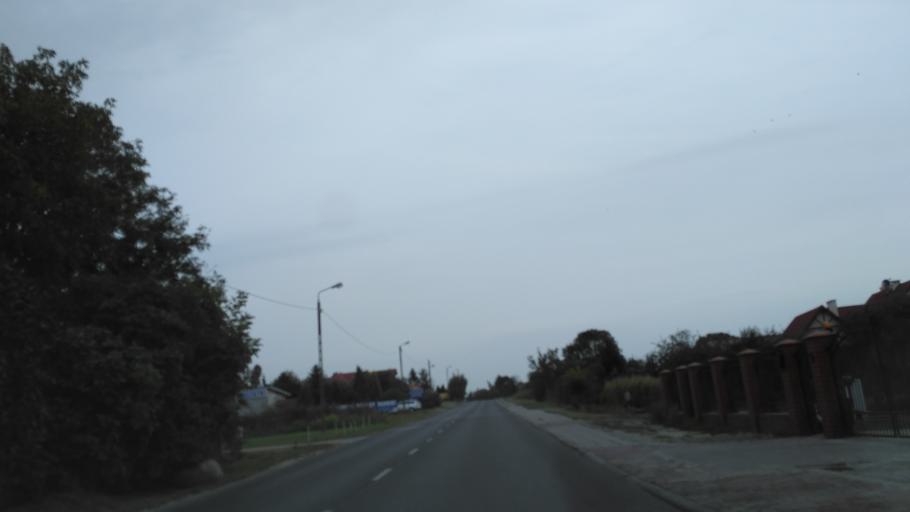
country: PL
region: Lublin Voivodeship
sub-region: Powiat lubelski
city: Lublin
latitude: 51.2179
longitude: 22.5898
